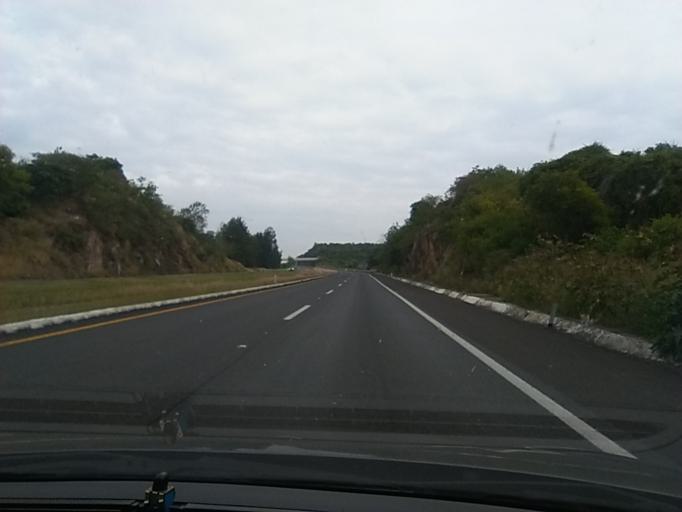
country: MX
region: Michoacan
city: Panindicuaro de la Reforma
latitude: 19.9697
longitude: -101.7167
